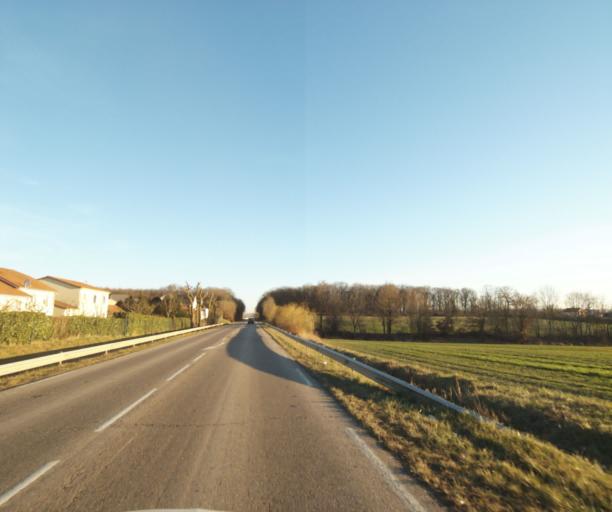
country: FR
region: Lorraine
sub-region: Departement de Meurthe-et-Moselle
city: Laneuveville-devant-Nancy
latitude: 48.6738
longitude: 6.2288
